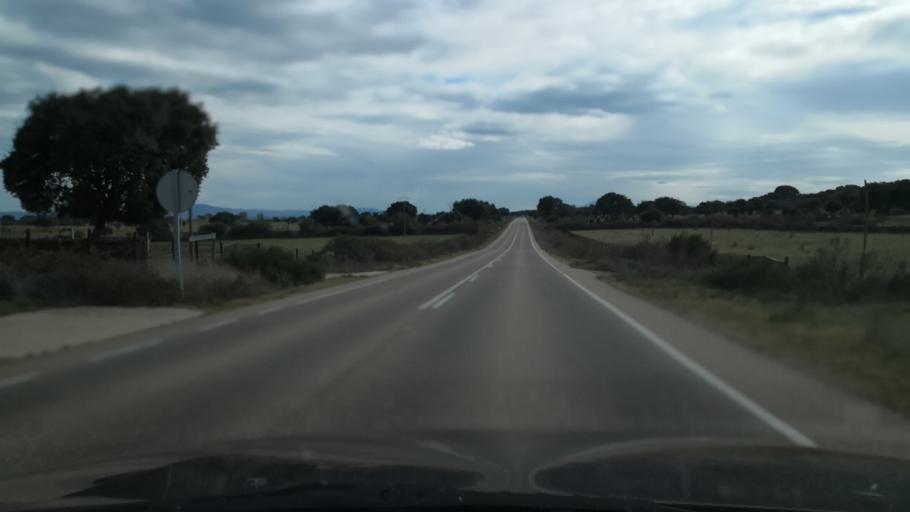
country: ES
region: Castille and Leon
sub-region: Provincia de Salamanca
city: Herguijuela de Ciudad Rodrigo
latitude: 40.4677
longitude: -6.5841
